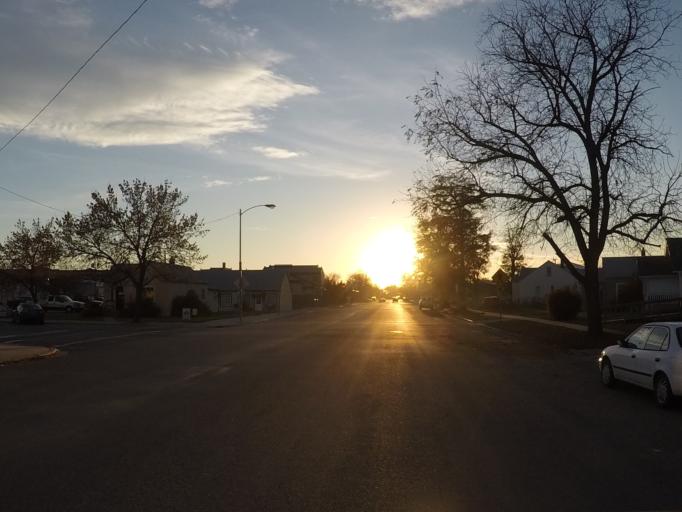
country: US
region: Montana
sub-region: Yellowstone County
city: Laurel
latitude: 45.6710
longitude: -108.7687
